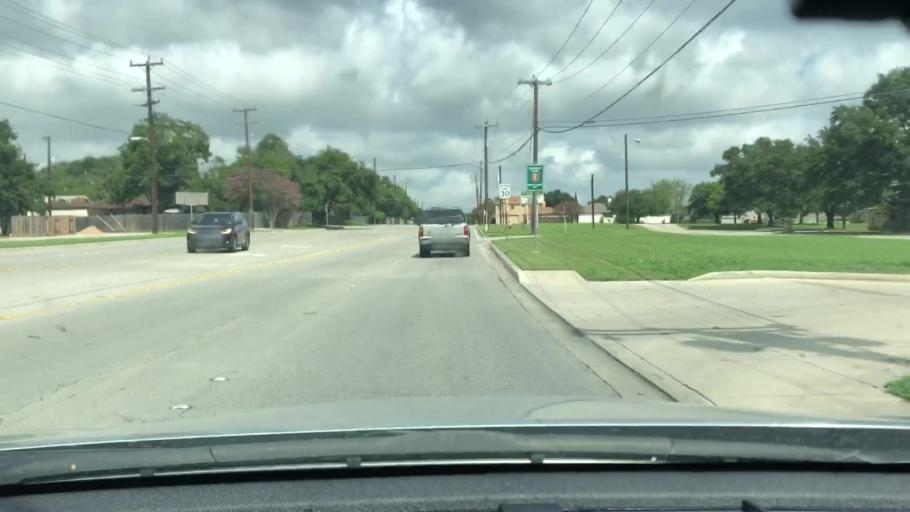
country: US
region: Texas
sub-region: Bexar County
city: Windcrest
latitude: 29.5111
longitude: -98.3716
